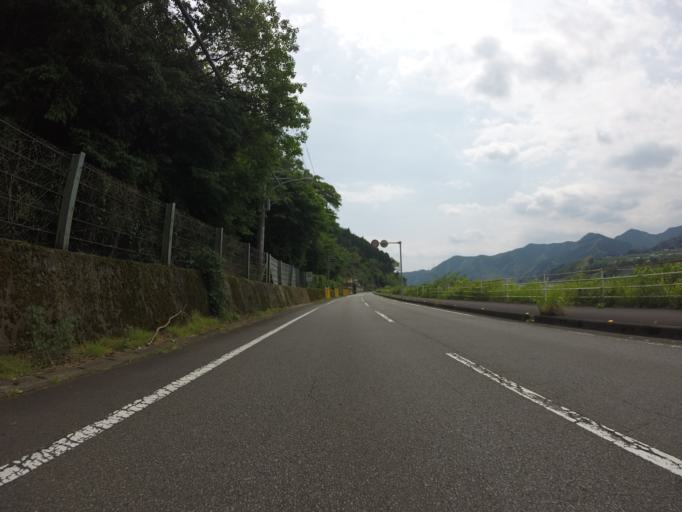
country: JP
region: Shizuoka
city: Shizuoka-shi
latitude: 35.0822
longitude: 138.3762
